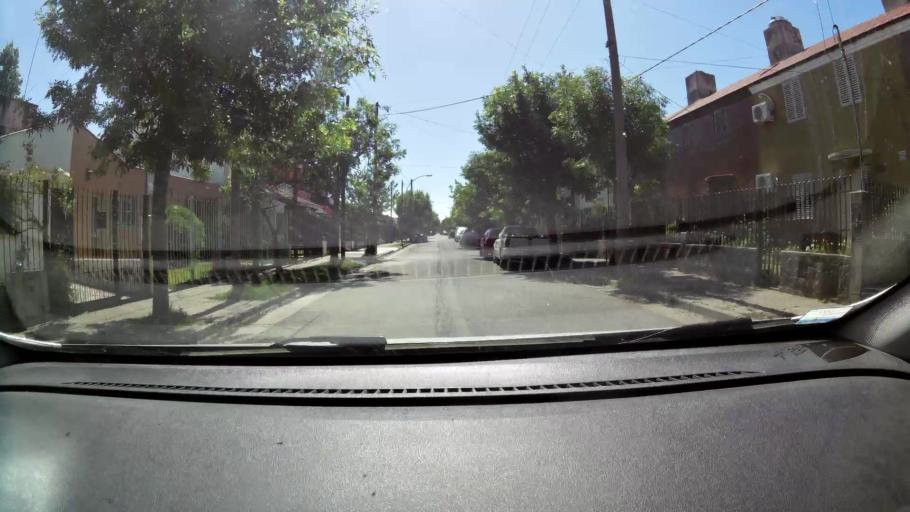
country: AR
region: Cordoba
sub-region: Departamento de Capital
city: Cordoba
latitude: -31.3757
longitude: -64.1577
